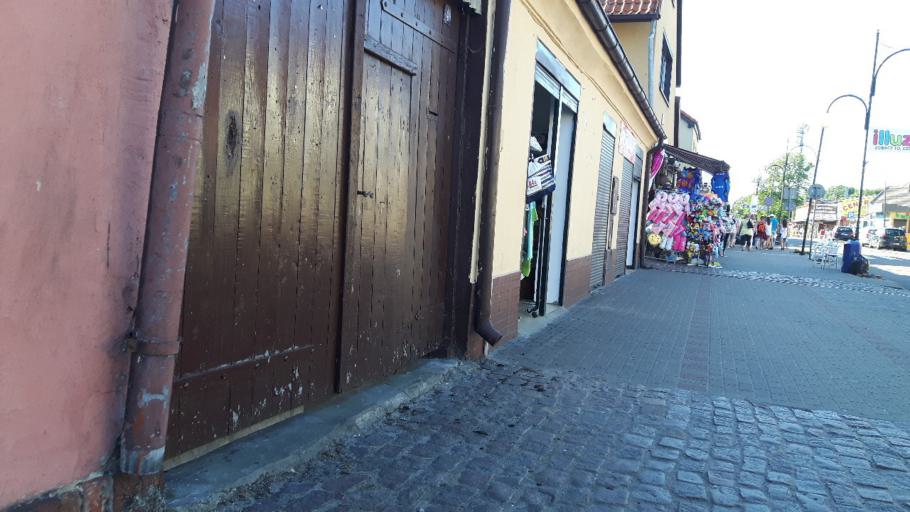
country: PL
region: Pomeranian Voivodeship
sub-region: Powiat leborski
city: Leba
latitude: 54.7592
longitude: 17.5555
